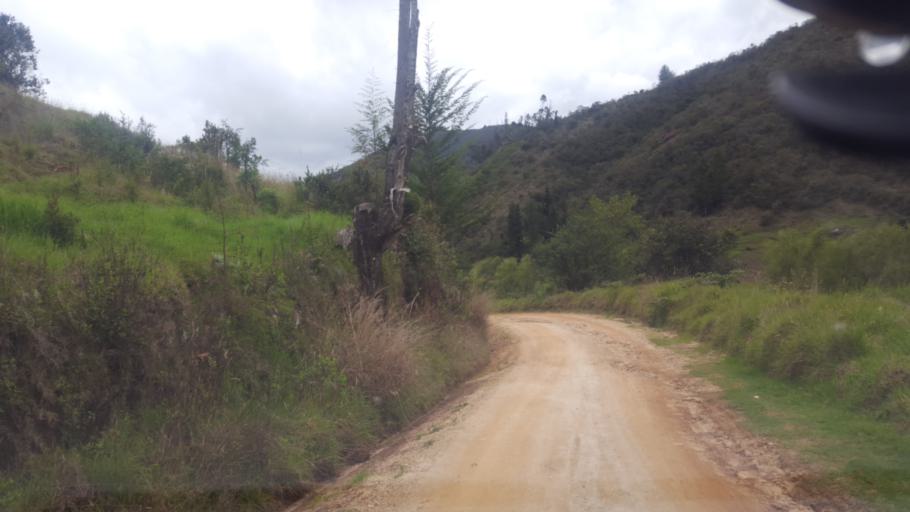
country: CO
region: Boyaca
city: Belen
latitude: 6.0153
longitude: -72.8735
